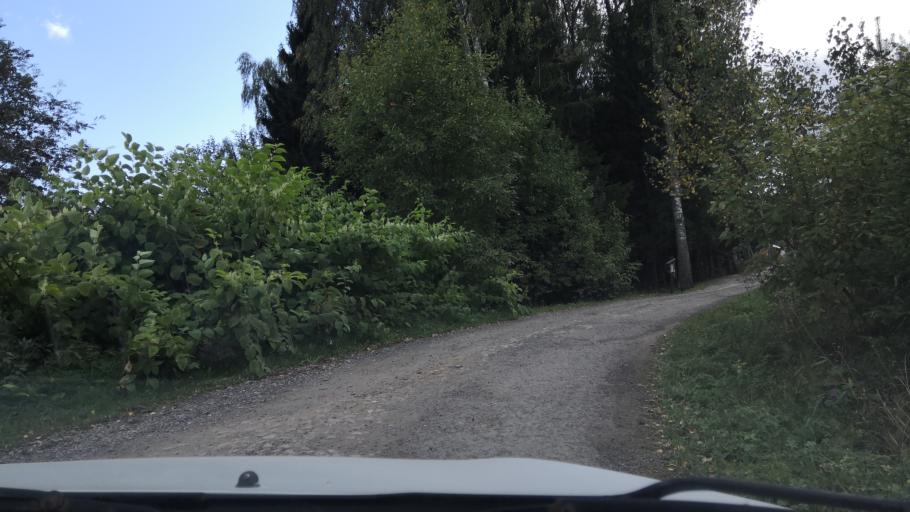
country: RU
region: Moskovskaya
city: Povarovo
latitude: 56.0560
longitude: 37.0207
